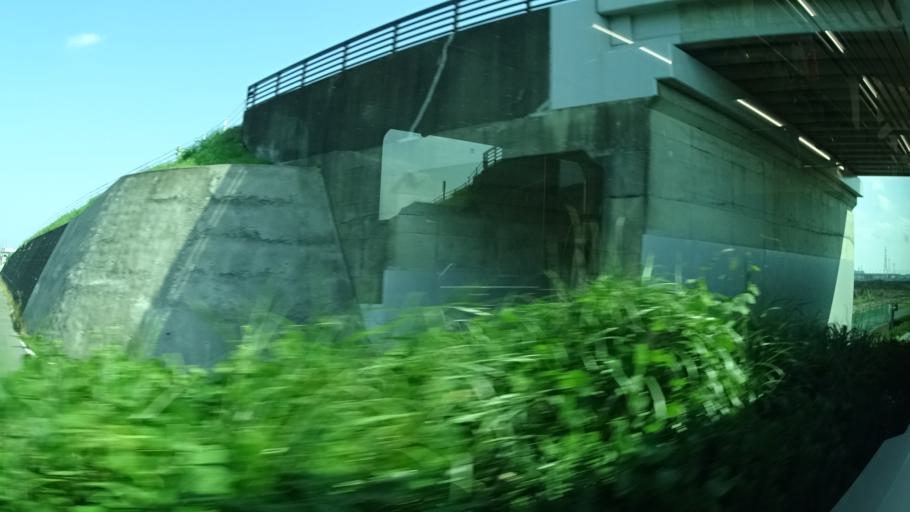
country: JP
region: Miyagi
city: Rifu
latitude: 38.2975
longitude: 140.9463
